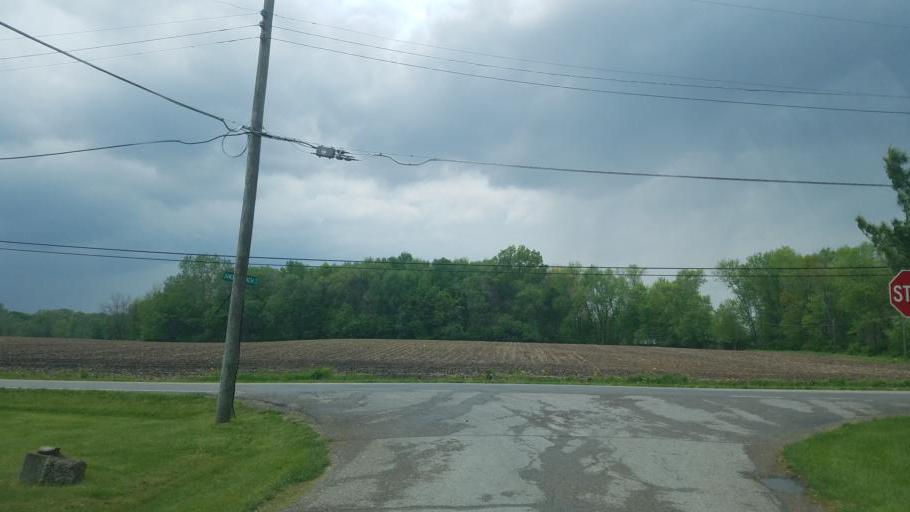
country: US
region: Ohio
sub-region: Fairfield County
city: Fairfield Beach
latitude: 39.9161
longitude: -82.4852
